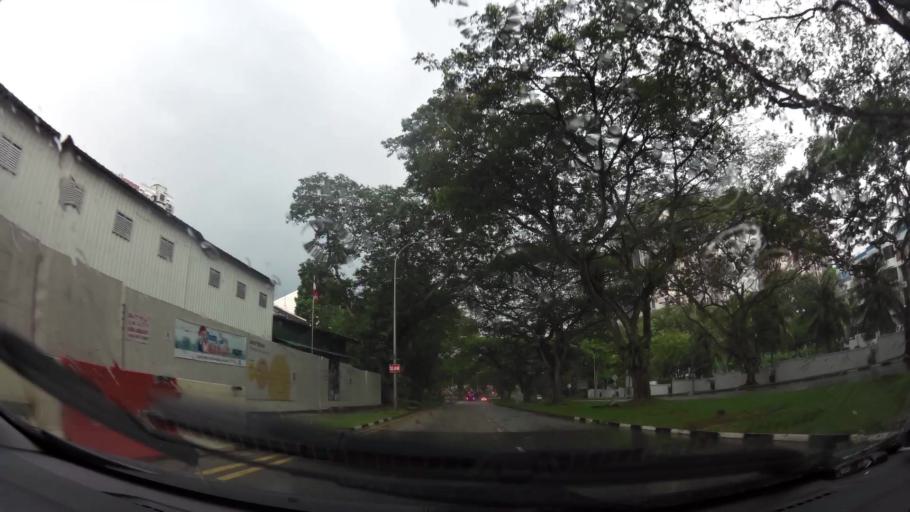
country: SG
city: Singapore
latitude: 1.3848
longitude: 103.8379
